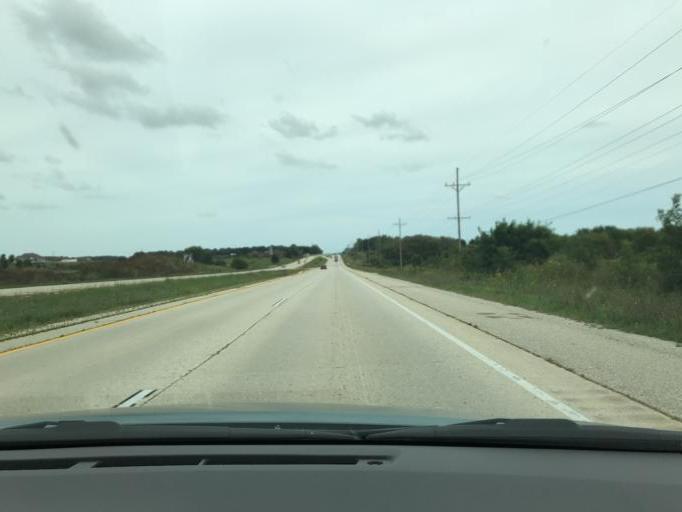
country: US
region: Wisconsin
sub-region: Kenosha County
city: Bristol
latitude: 42.5673
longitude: -87.9908
